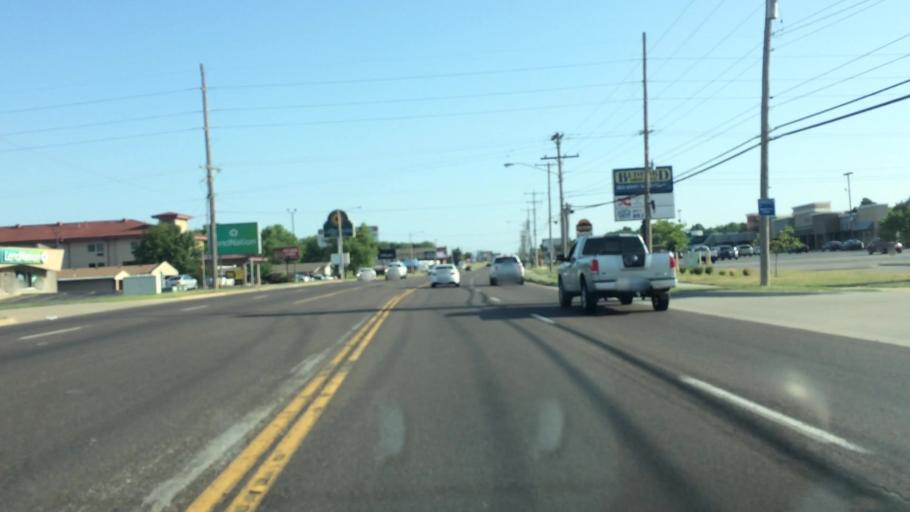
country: US
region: Missouri
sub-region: Greene County
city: Springfield
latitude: 37.1670
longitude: -93.2955
